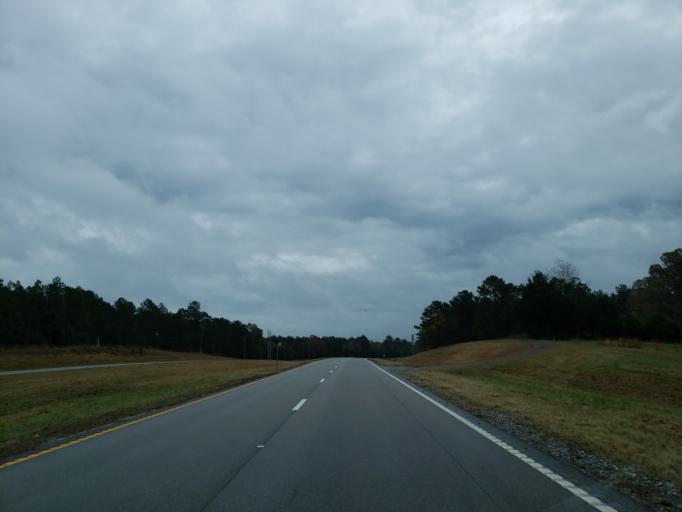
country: US
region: Mississippi
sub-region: Wayne County
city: Waynesboro
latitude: 31.6959
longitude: -88.7280
